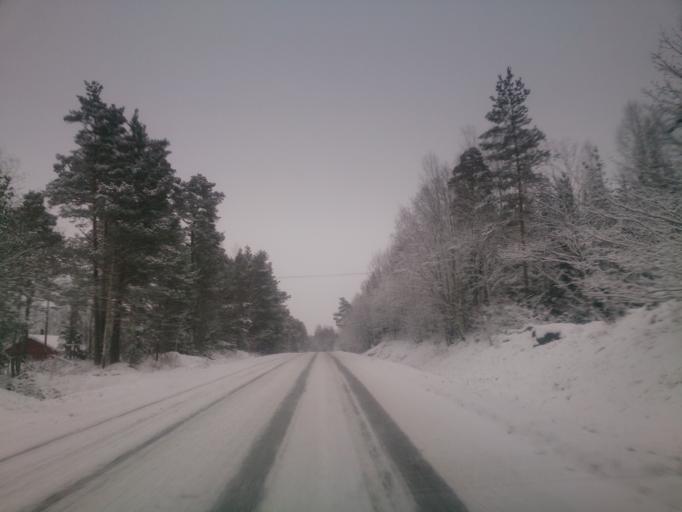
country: SE
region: OEstergoetland
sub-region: Finspangs Kommun
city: Finspang
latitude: 58.6240
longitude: 15.8192
